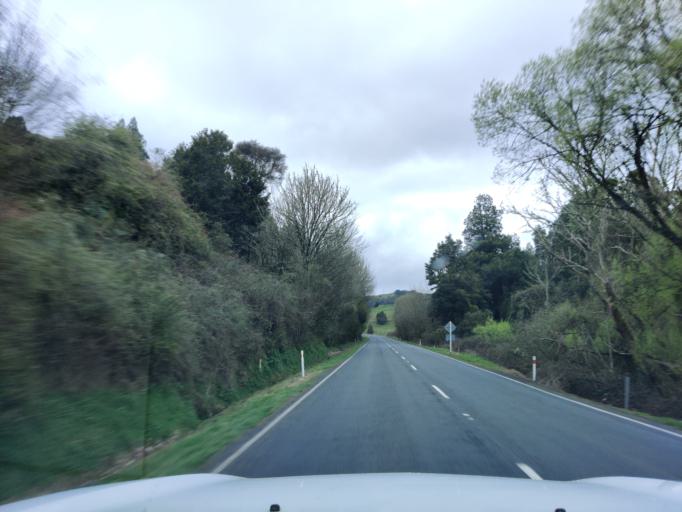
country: NZ
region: Waikato
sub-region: Otorohanga District
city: Otorohanga
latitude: -38.5965
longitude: 175.2187
